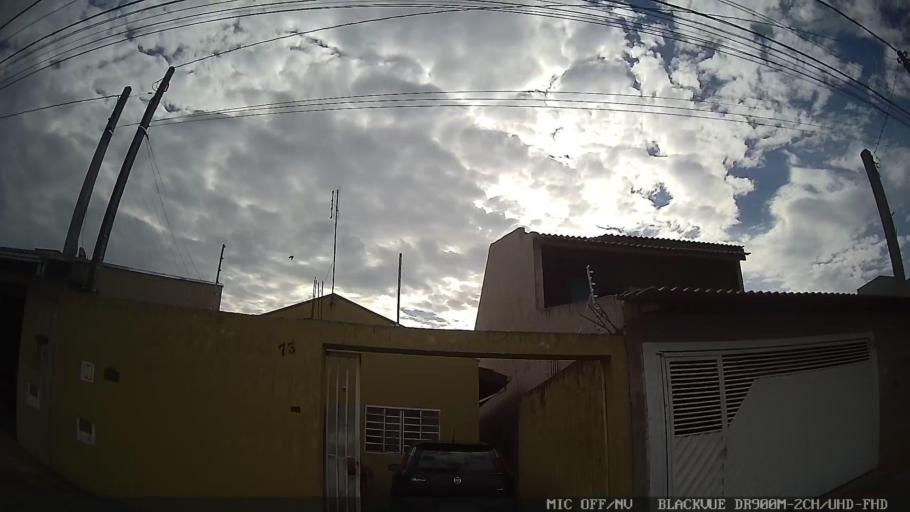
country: BR
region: Sao Paulo
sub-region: Salto
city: Salto
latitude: -23.1829
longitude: -47.2731
